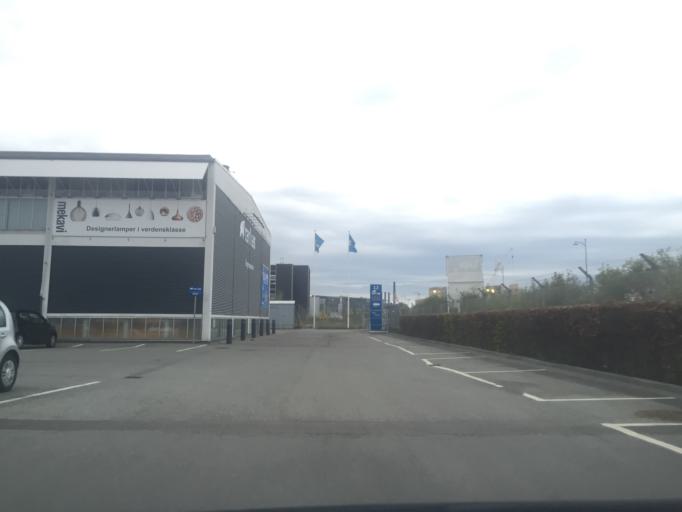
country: DK
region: Capital Region
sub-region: Frederiksberg Kommune
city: Frederiksberg
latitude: 55.6442
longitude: 12.5397
